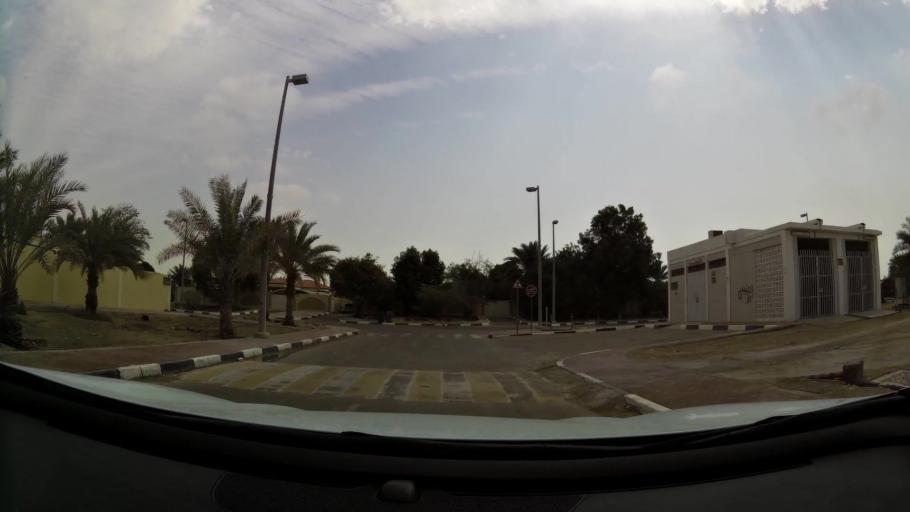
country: AE
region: Abu Dhabi
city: Abu Dhabi
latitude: 24.5217
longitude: 54.6814
